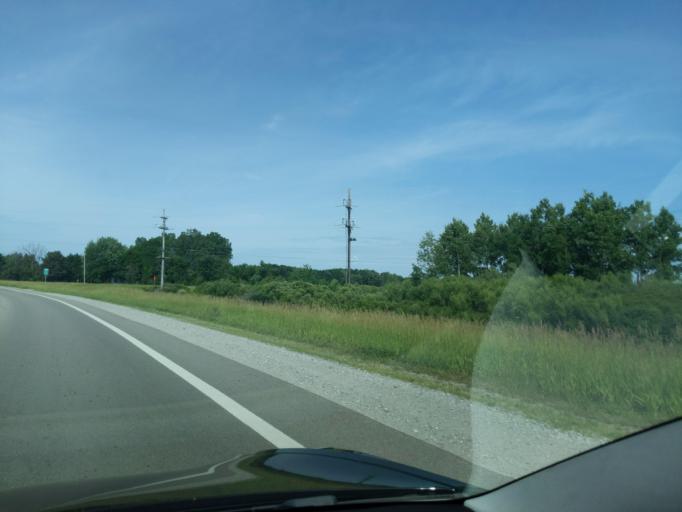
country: US
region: Michigan
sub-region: Newaygo County
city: Fremont
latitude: 43.4247
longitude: -86.0415
